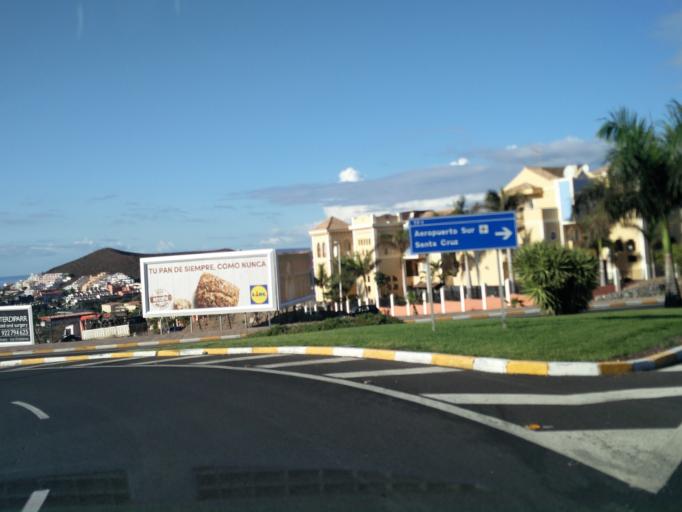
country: ES
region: Canary Islands
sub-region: Provincia de Santa Cruz de Tenerife
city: Playa de las Americas
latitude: 28.0637
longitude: -16.7112
